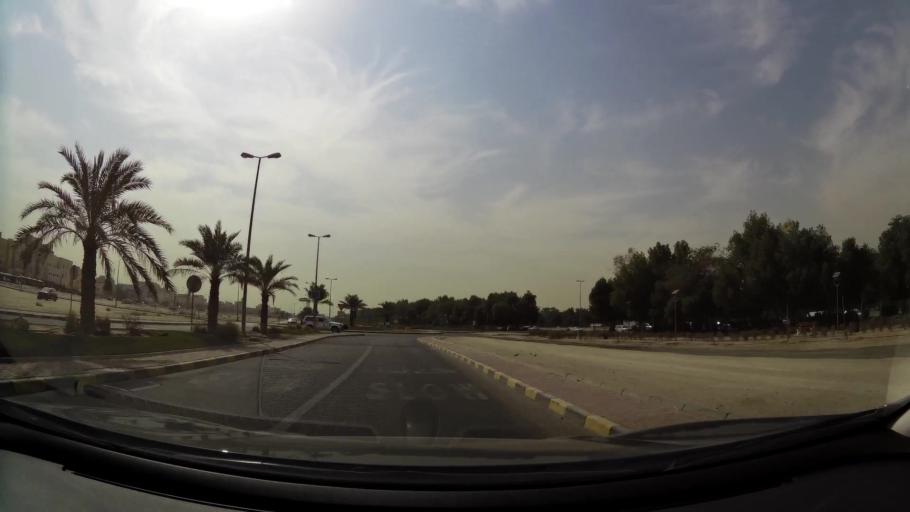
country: KW
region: Al Farwaniyah
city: Janub as Surrah
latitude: 29.2772
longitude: 47.9872
